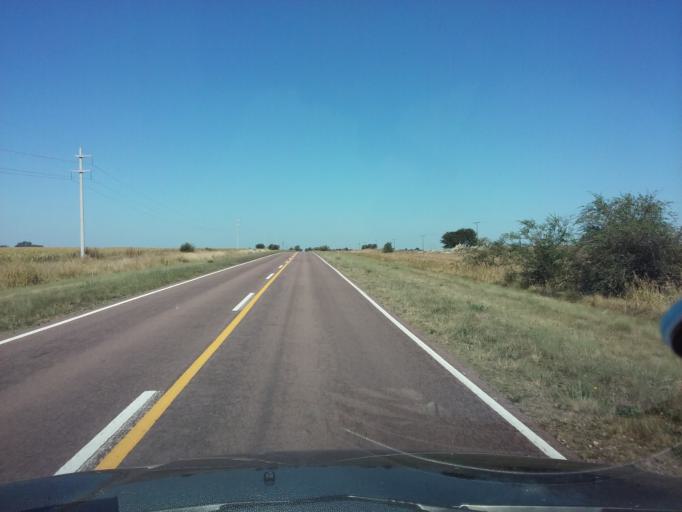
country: AR
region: La Pampa
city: Uriburu
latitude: -36.3831
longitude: -63.9432
